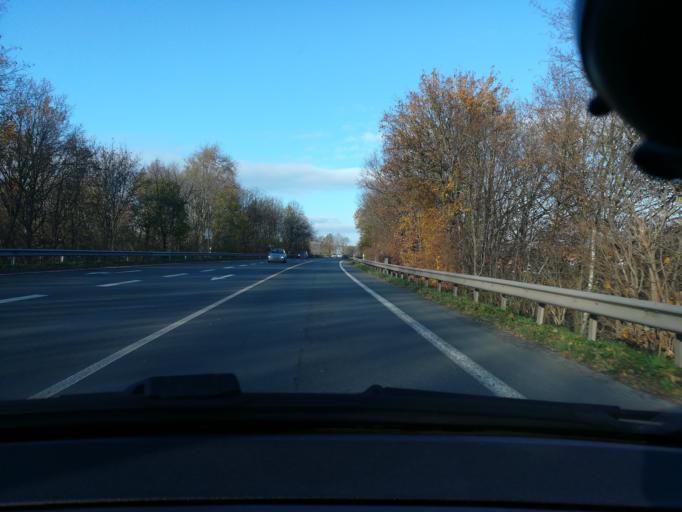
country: DE
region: North Rhine-Westphalia
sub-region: Regierungsbezirk Detmold
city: Petershagen
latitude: 52.3377
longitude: 8.9618
